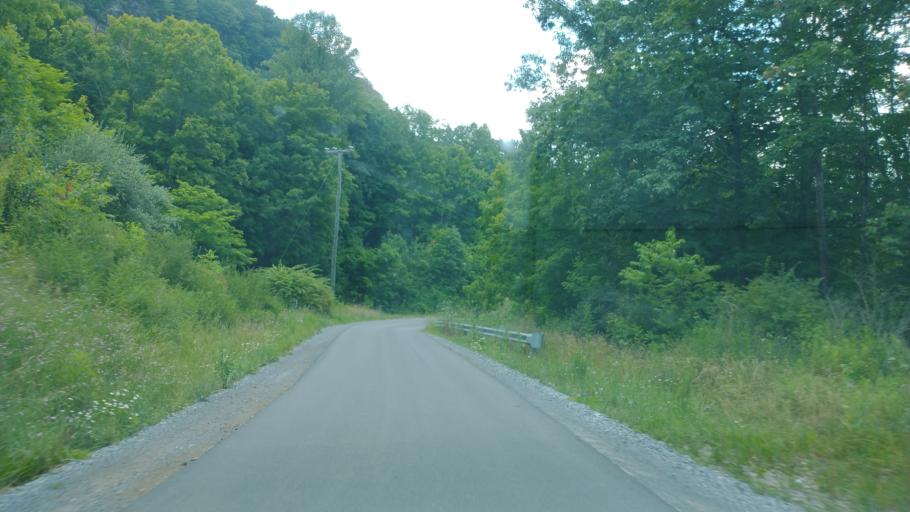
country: US
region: West Virginia
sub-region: Mercer County
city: Athens
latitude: 37.4609
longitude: -81.0636
